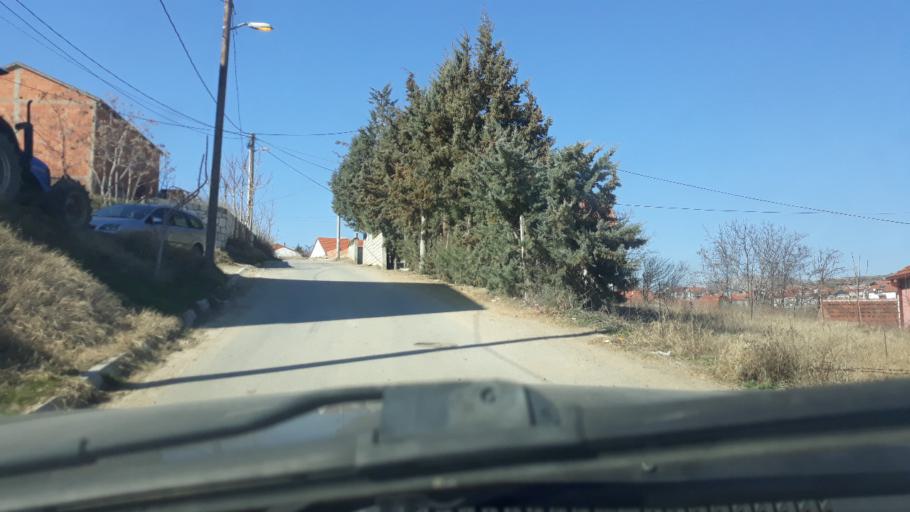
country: MK
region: Veles
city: Gorno Orizari
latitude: 41.6817
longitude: 21.7345
